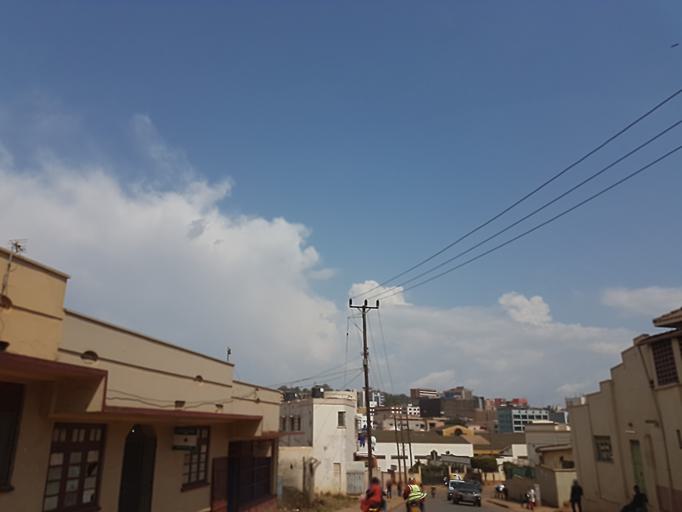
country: UG
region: Central Region
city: Kampala Central Division
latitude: 0.3181
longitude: 32.5697
